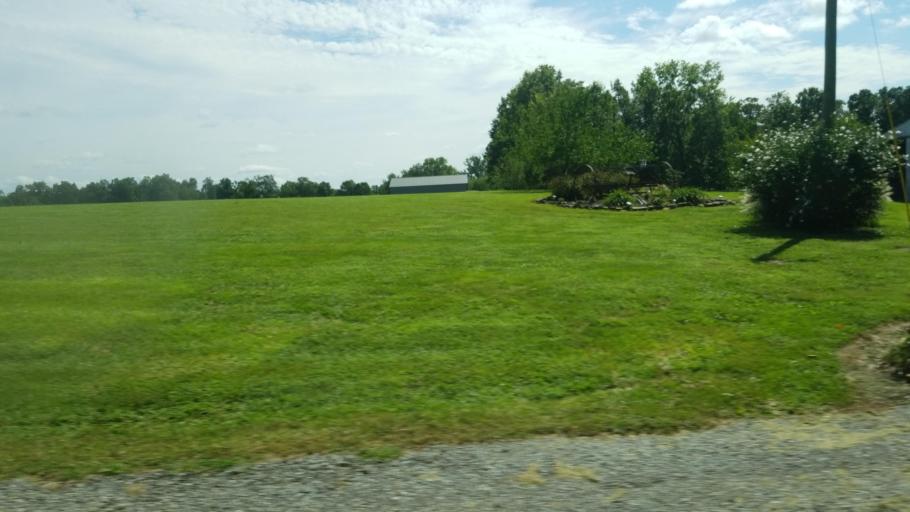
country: US
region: Illinois
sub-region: Williamson County
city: Johnston City
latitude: 37.7902
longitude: -88.8237
